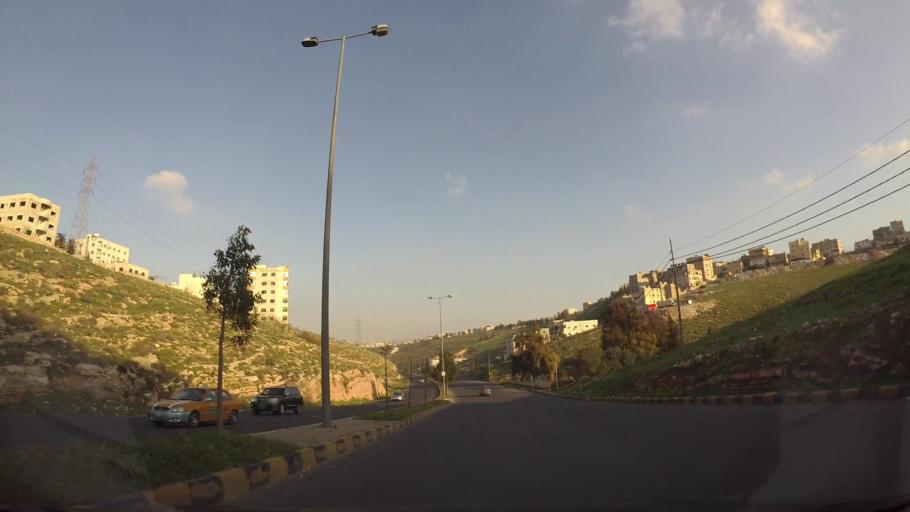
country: JO
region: Amman
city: Amman
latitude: 31.9836
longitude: 35.9572
